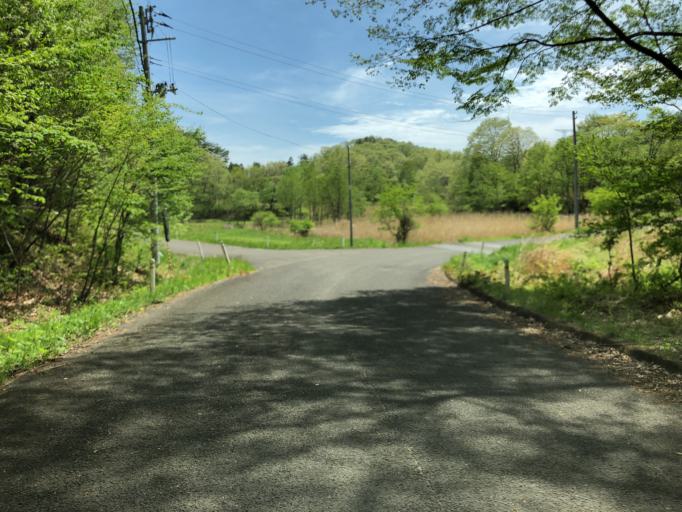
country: JP
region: Miyagi
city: Marumori
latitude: 37.7052
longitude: 140.7794
